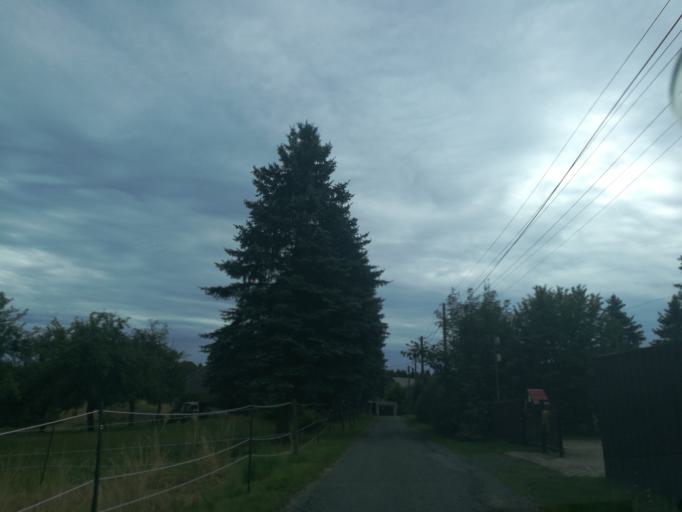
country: DE
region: Saxony
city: Adorf
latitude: 50.3079
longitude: 12.2784
